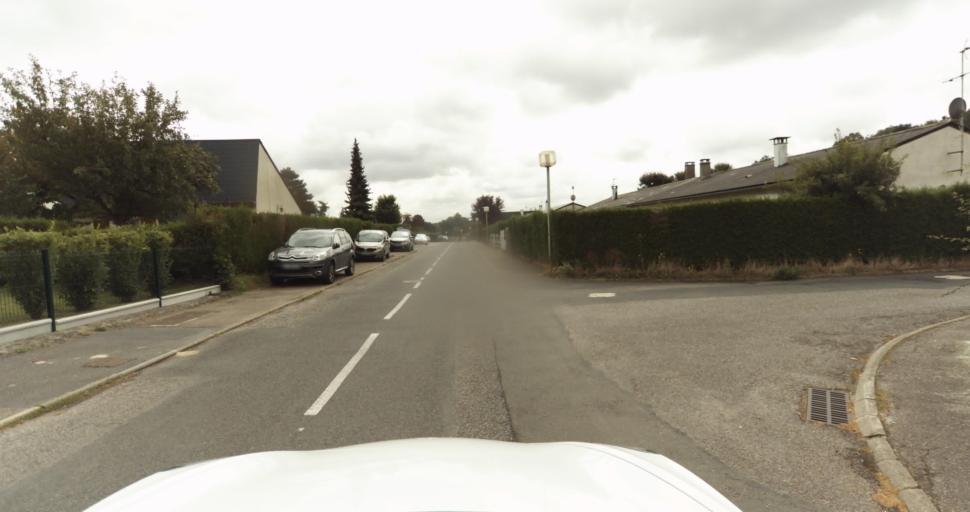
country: FR
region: Haute-Normandie
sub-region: Departement de l'Eure
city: Saint-Sebastien-de-Morsent
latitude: 49.0075
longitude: 1.0933
